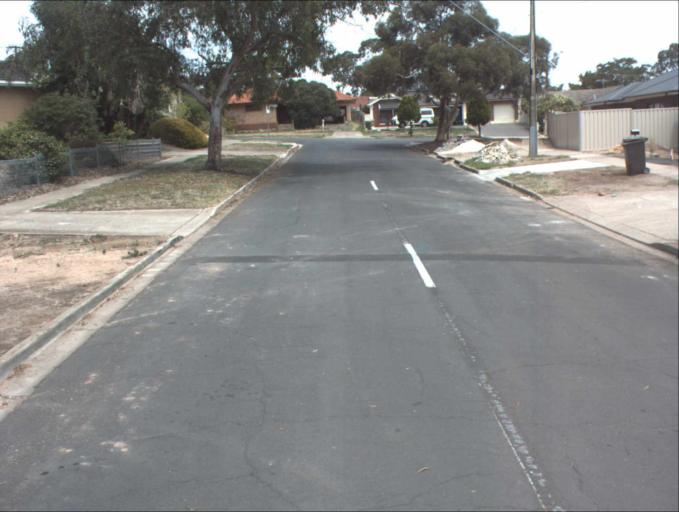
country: AU
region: South Australia
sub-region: Port Adelaide Enfield
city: Enfield
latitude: -34.8488
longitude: 138.6138
